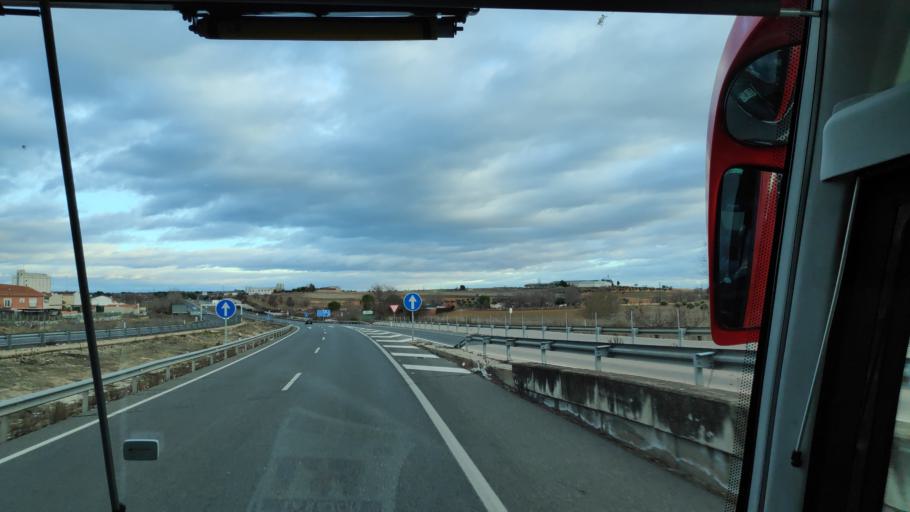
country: ES
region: Madrid
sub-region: Provincia de Madrid
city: Villarejo de Salvanes
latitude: 40.1651
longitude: -3.2810
